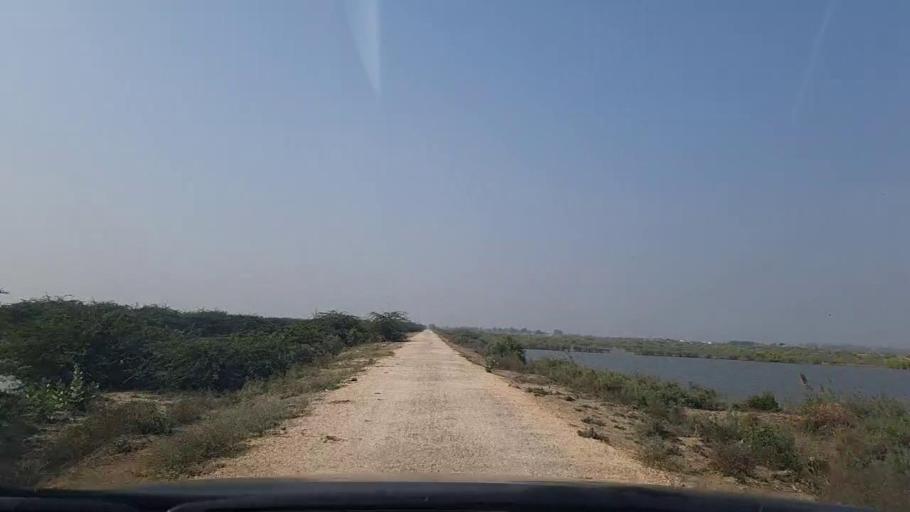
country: PK
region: Sindh
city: Mirpur Sakro
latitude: 24.5750
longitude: 67.7628
